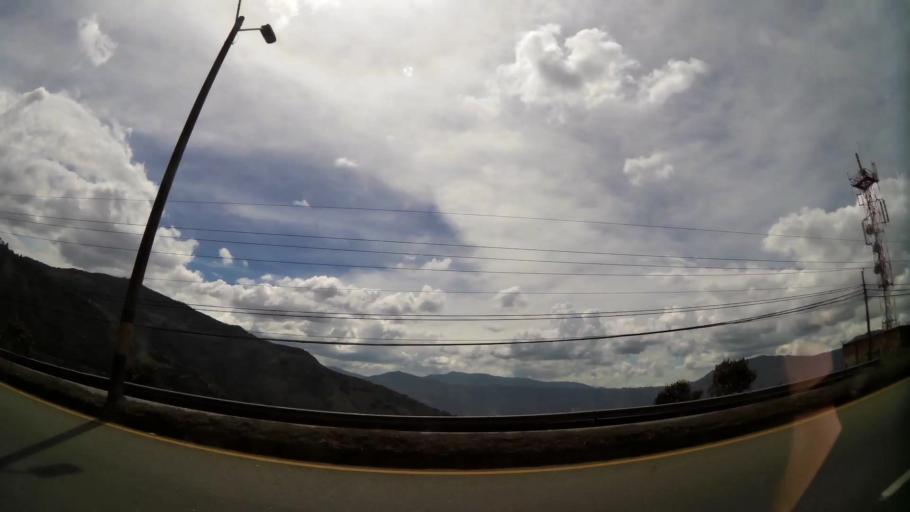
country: CO
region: Antioquia
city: Municipio de Copacabana
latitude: 6.3227
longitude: -75.4899
